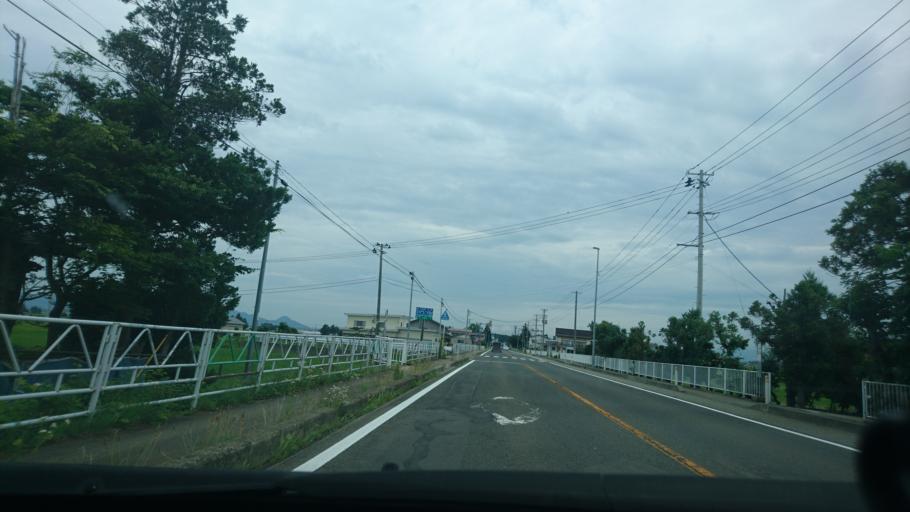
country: JP
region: Akita
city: Omagari
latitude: 39.4056
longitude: 140.5587
